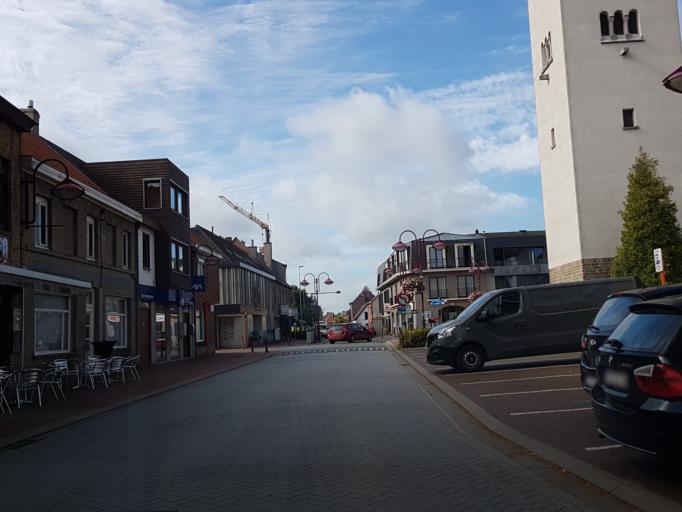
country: BE
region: Flanders
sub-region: Provincie Oost-Vlaanderen
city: Nevele
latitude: 51.0570
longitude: 3.5735
